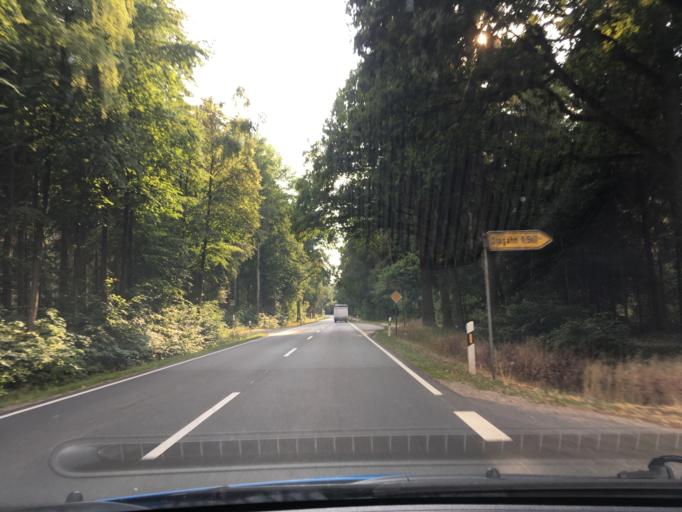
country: DE
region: Lower Saxony
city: Karwitz
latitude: 53.0806
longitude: 10.9749
